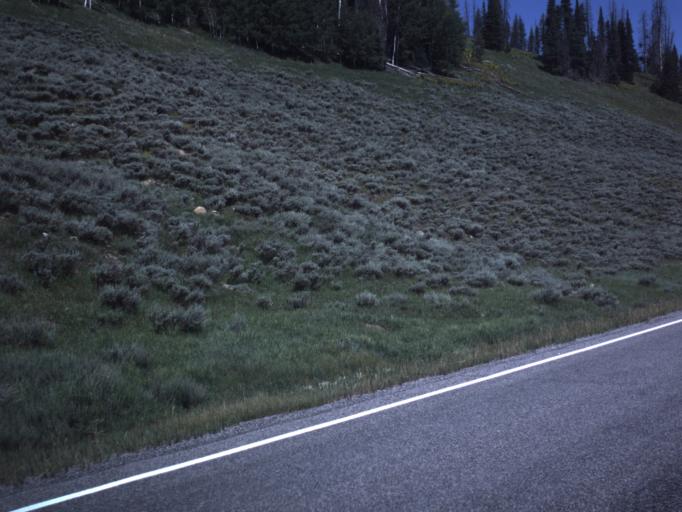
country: US
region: Utah
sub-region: Sanpete County
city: Fairview
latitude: 39.6776
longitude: -111.2435
